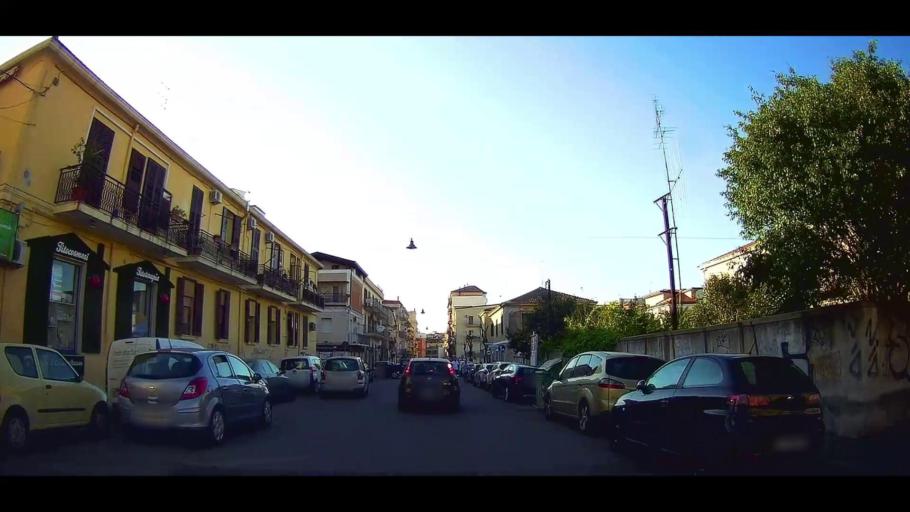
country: IT
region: Calabria
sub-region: Provincia di Crotone
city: Crotone
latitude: 39.0784
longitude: 17.1271
